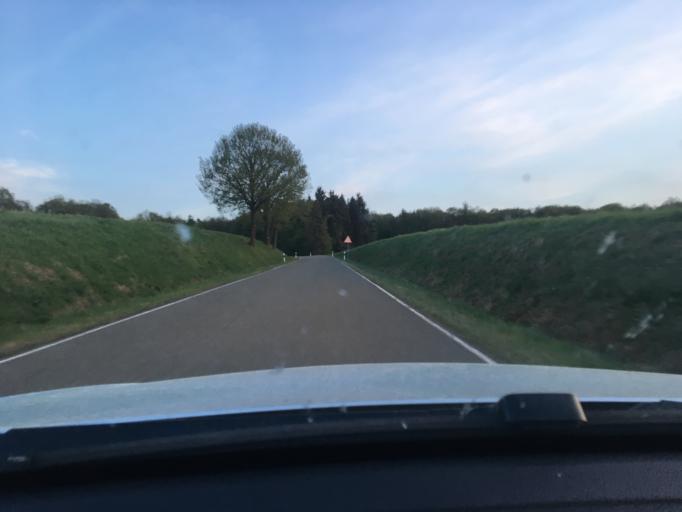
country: DE
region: Rheinland-Pfalz
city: Kriegsfeld
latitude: 49.7041
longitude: 7.9119
